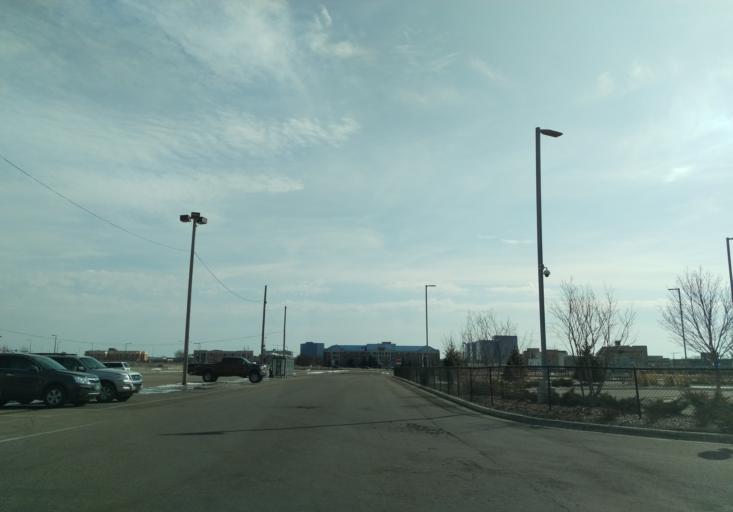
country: US
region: Minnesota
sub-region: Hennepin County
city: Richfield
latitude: 44.8582
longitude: -93.2420
